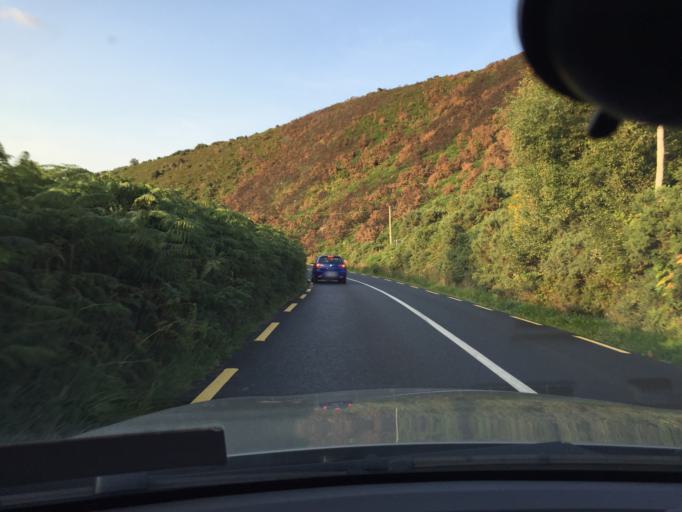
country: IE
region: Leinster
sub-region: Wicklow
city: Rathdrum
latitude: 53.0353
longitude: -6.2492
